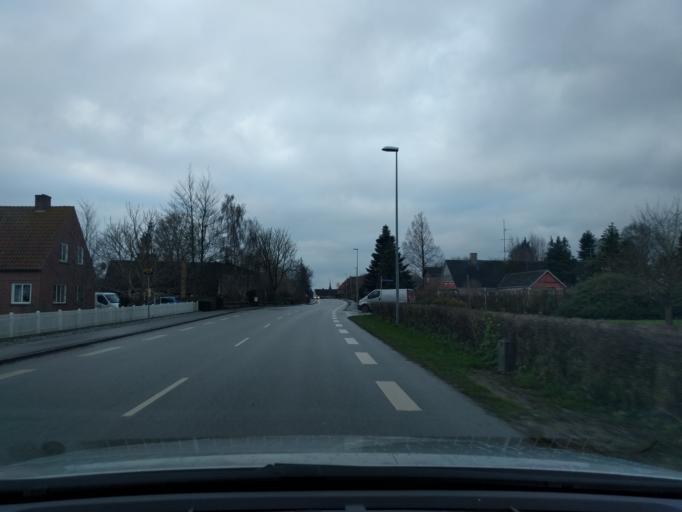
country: DK
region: Zealand
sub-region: Guldborgsund Kommune
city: Stubbekobing
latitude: 54.8657
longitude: 12.0209
